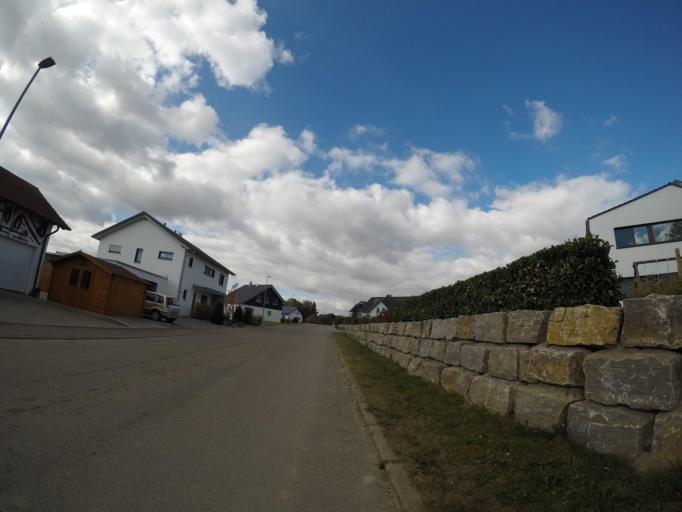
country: DE
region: Baden-Wuerttemberg
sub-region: Tuebingen Region
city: Unterstadion
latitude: 48.2014
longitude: 9.6959
